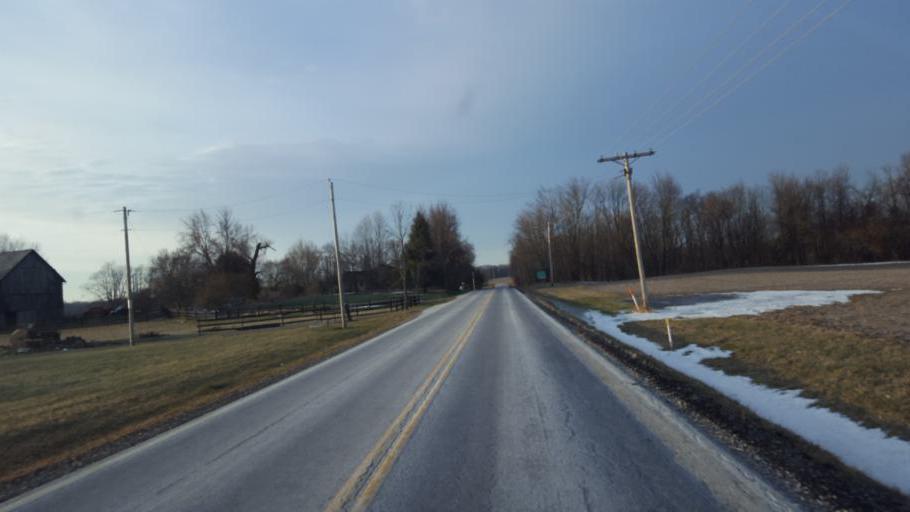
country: US
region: Ohio
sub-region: Knox County
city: Centerburg
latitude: 40.4277
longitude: -82.6991
